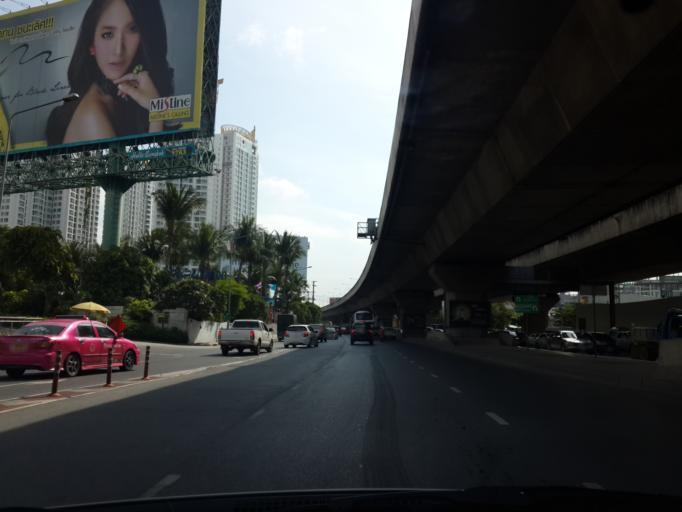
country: TH
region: Bangkok
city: Huai Khwang
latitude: 13.7525
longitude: 100.5721
